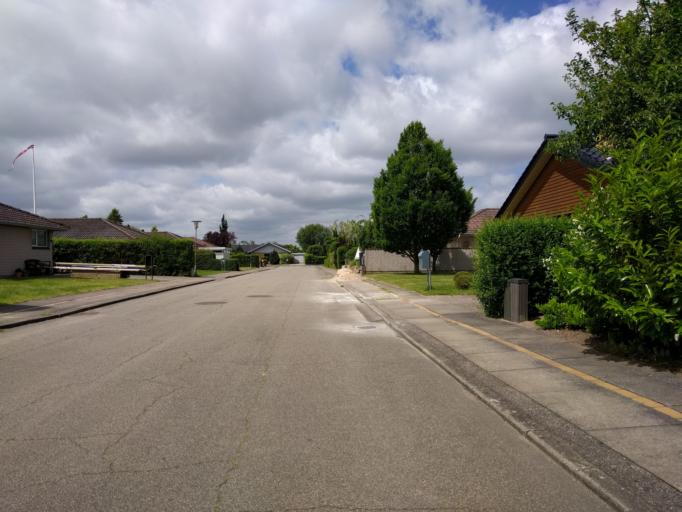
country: DK
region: South Denmark
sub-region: Odense Kommune
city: Bullerup
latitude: 55.4330
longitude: 10.4935
